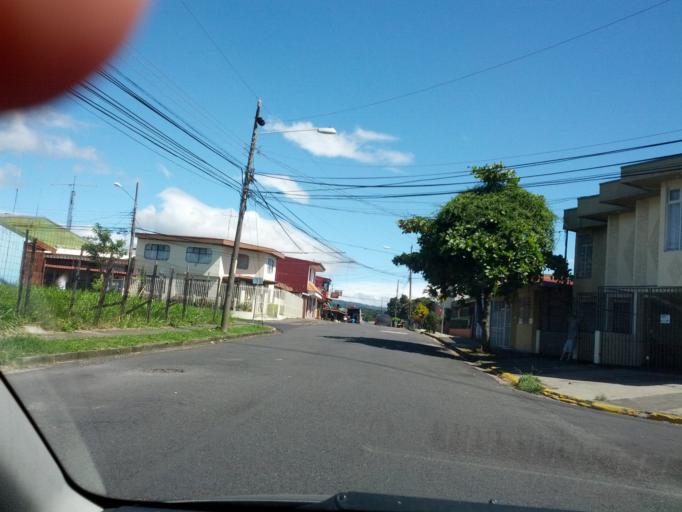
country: CR
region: Alajuela
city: Alajuela
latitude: 10.0150
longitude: -84.2057
